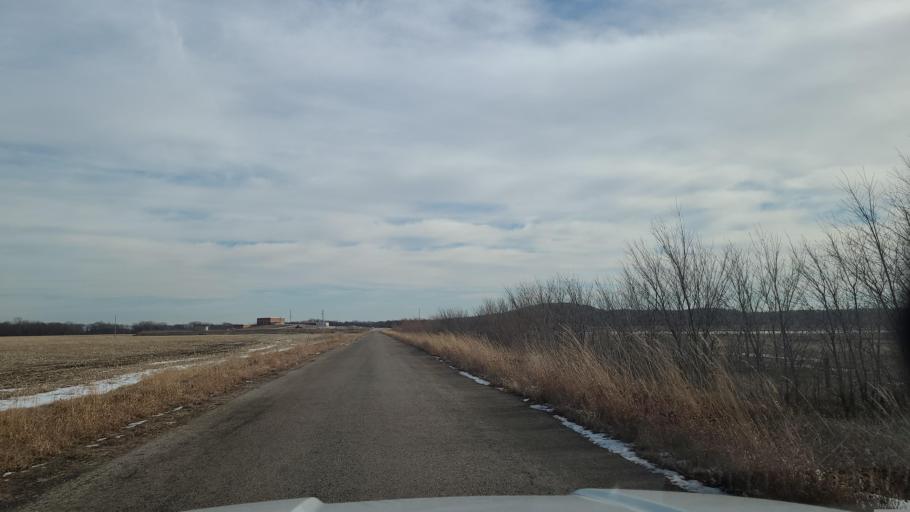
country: US
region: Kansas
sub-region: Douglas County
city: Lawrence
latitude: 38.9100
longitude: -95.2103
